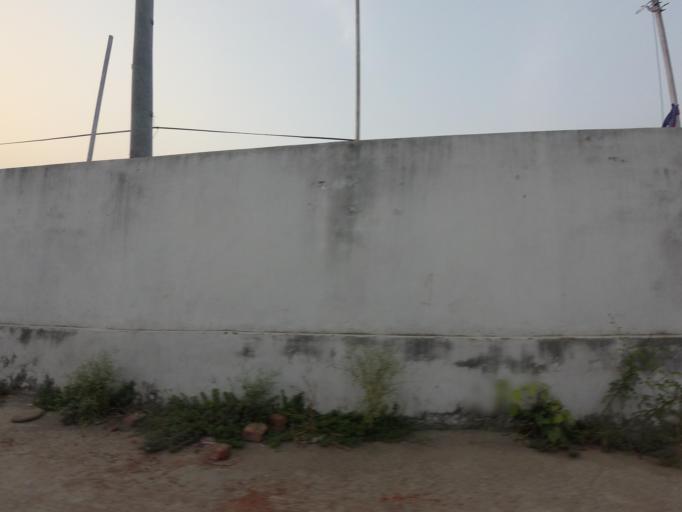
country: NP
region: Western Region
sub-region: Lumbini Zone
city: Bhairahawa
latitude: 27.5025
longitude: 83.4577
